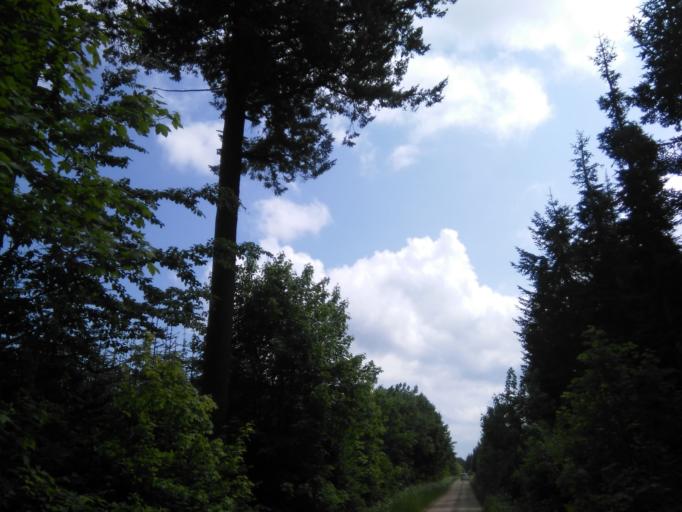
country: DK
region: Central Jutland
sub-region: Favrskov Kommune
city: Hinnerup
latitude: 56.2769
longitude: 9.9863
